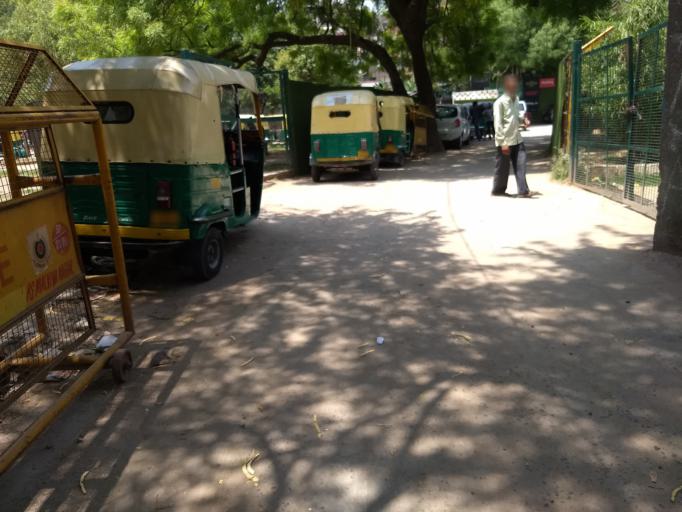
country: IN
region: NCT
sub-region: New Delhi
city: New Delhi
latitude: 28.5299
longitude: 77.2165
